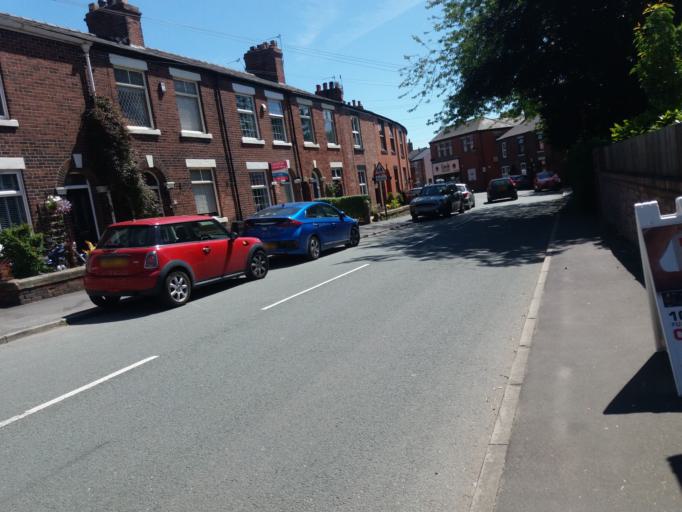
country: GB
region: England
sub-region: Lancashire
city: Croston
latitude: 53.6620
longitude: -2.7753
